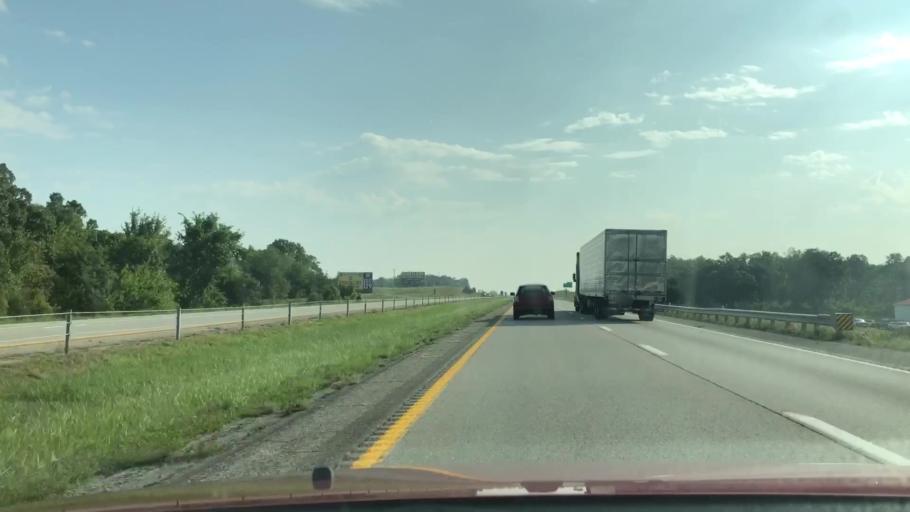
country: US
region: Missouri
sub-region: Laclede County
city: Lebanon
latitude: 37.5874
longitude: -92.7368
